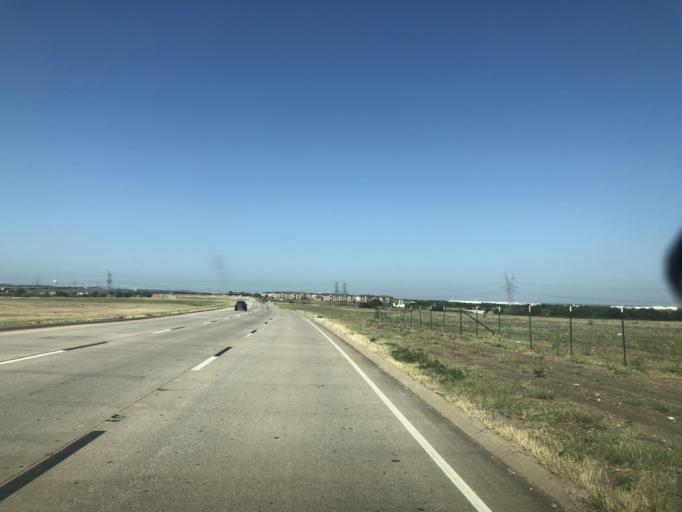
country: US
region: Texas
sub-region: Tarrant County
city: Keller
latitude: 32.9704
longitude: -97.2850
